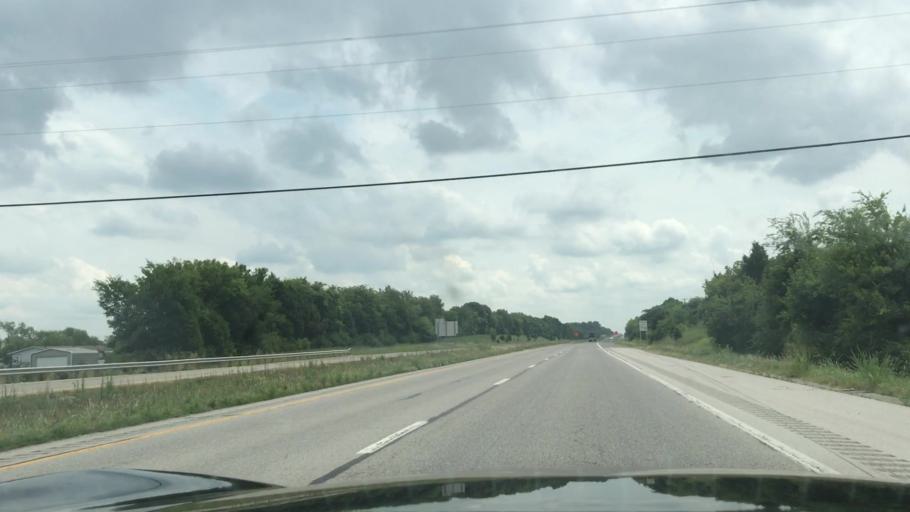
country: US
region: Kentucky
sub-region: Warren County
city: Bowling Green
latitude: 36.9883
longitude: -86.5032
